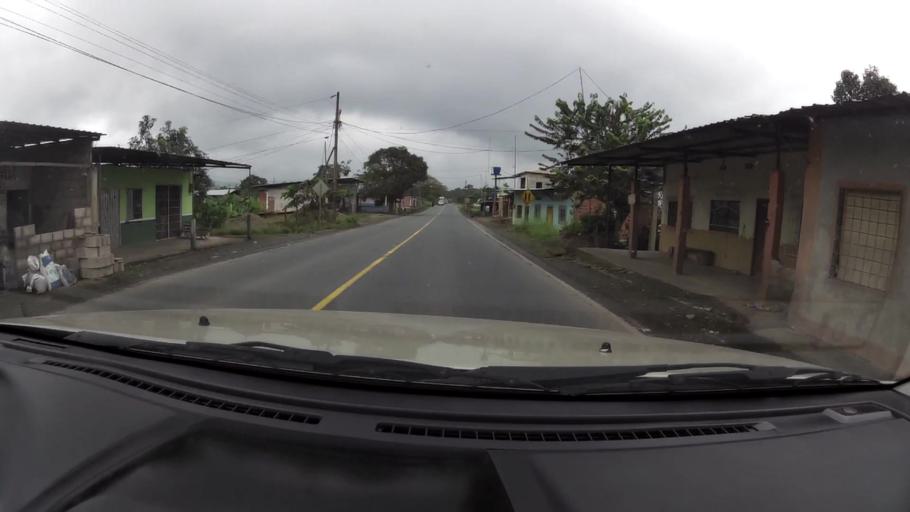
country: EC
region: Guayas
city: Balao
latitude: -2.9799
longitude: -79.7261
